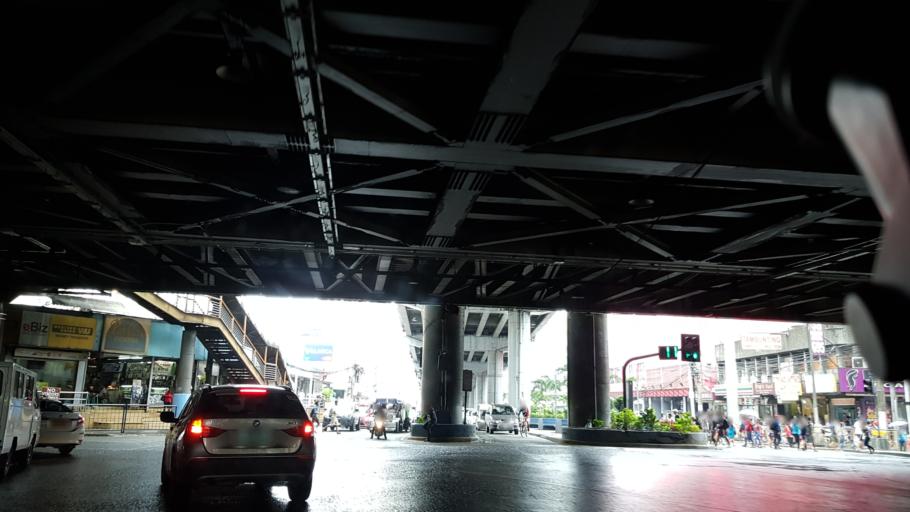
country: PH
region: Metro Manila
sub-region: Pasig
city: Pasig City
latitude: 14.5811
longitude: 121.0540
